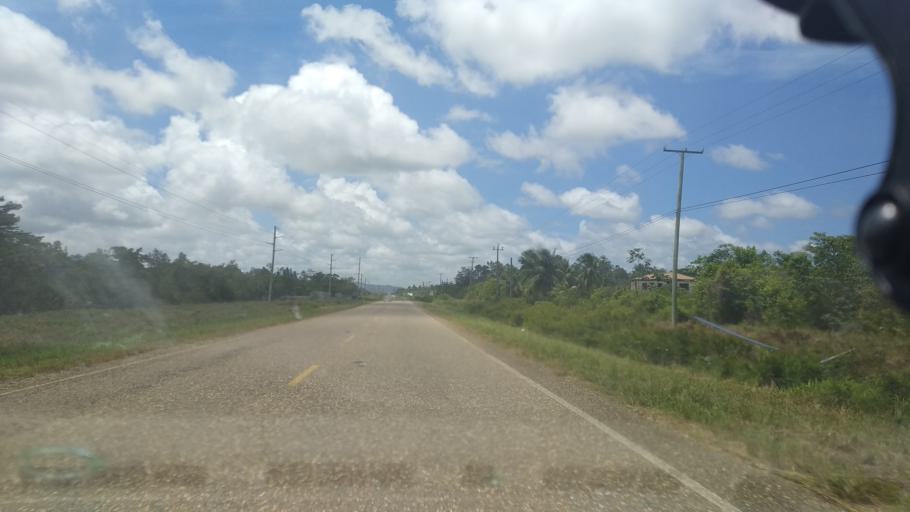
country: BZ
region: Stann Creek
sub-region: Dangriga
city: Dangriga
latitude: 16.8487
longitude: -88.3453
